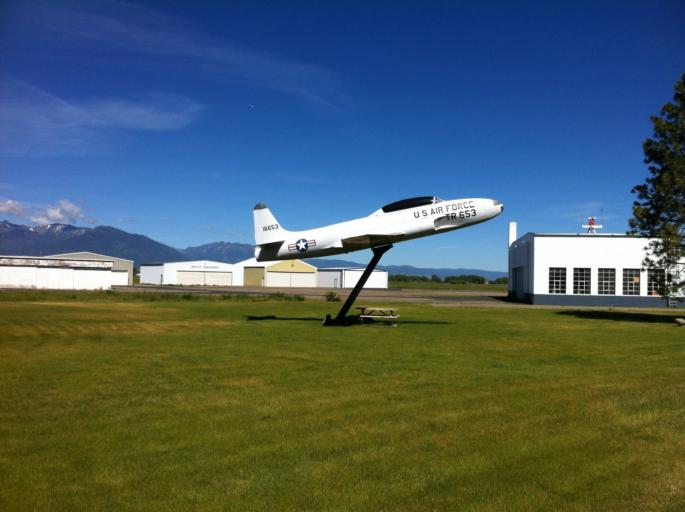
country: US
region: Oregon
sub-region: Baker County
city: Baker City
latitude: 44.8337
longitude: -117.8093
